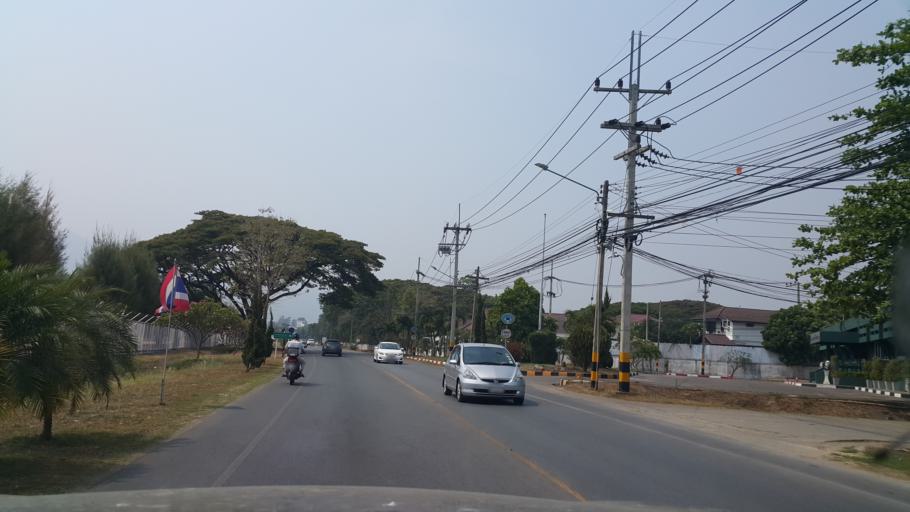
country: TH
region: Chiang Mai
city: Chiang Mai
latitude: 18.7827
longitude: 98.9656
